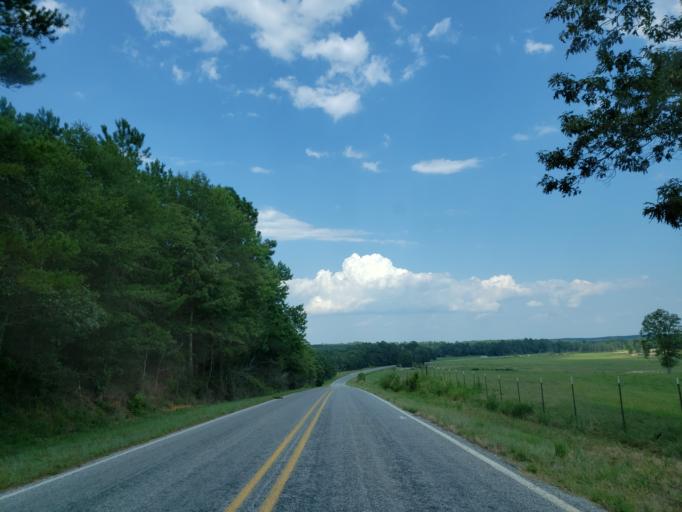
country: US
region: Mississippi
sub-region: Jones County
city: Ellisville
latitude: 31.6236
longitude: -89.3664
